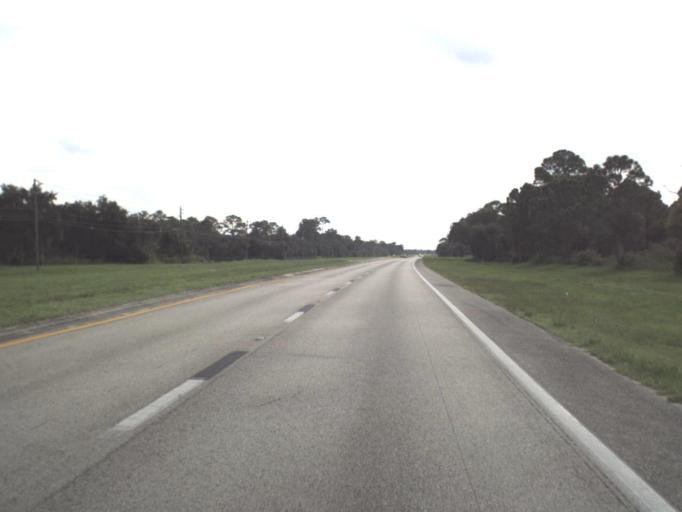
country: US
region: Florida
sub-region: Lee County
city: Alva
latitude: 26.7129
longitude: -81.6550
